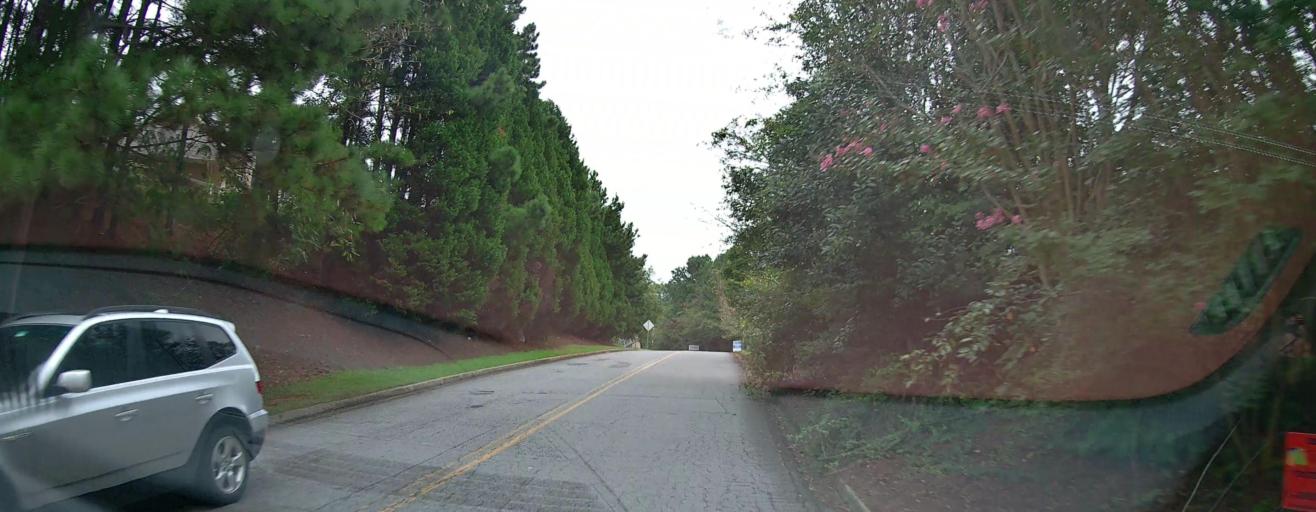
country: US
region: Georgia
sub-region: Bibb County
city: Macon
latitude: 32.8663
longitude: -83.6941
